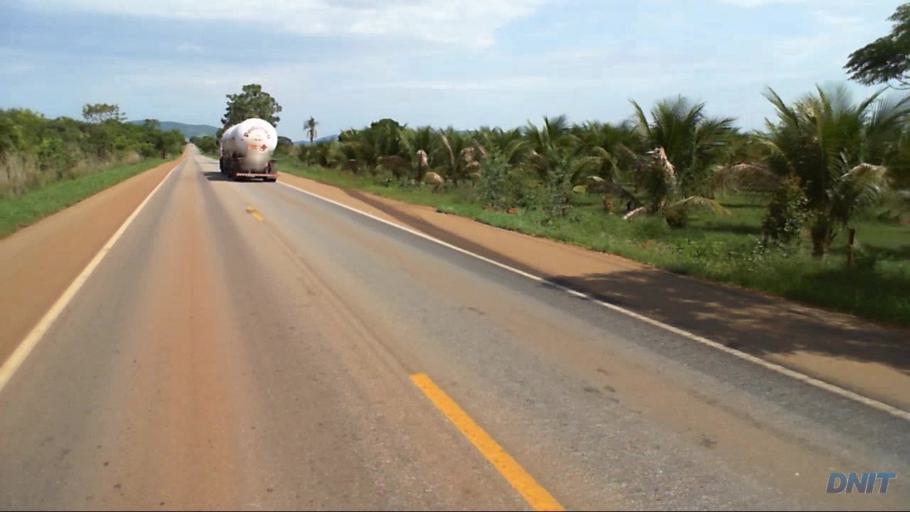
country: BR
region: Goias
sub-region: Barro Alto
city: Barro Alto
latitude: -15.0811
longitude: -48.8623
